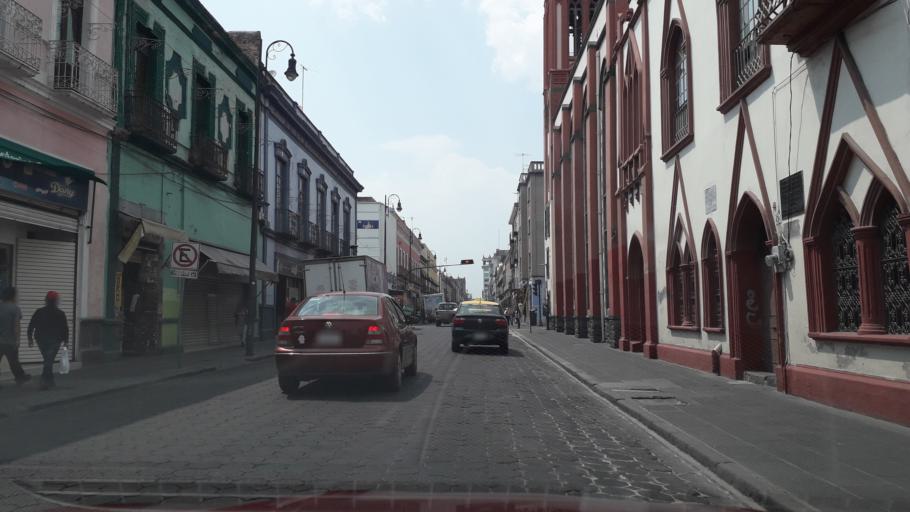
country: MX
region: Puebla
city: Puebla
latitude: 19.0465
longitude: -98.2007
